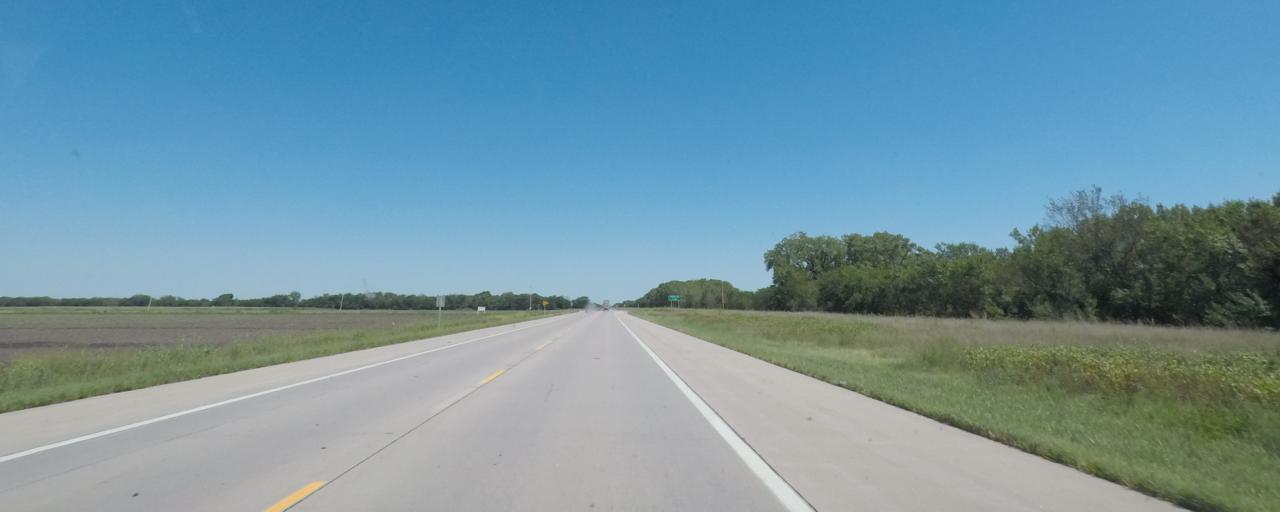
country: US
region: Kansas
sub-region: Chase County
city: Cottonwood Falls
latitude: 38.4069
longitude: -96.3767
